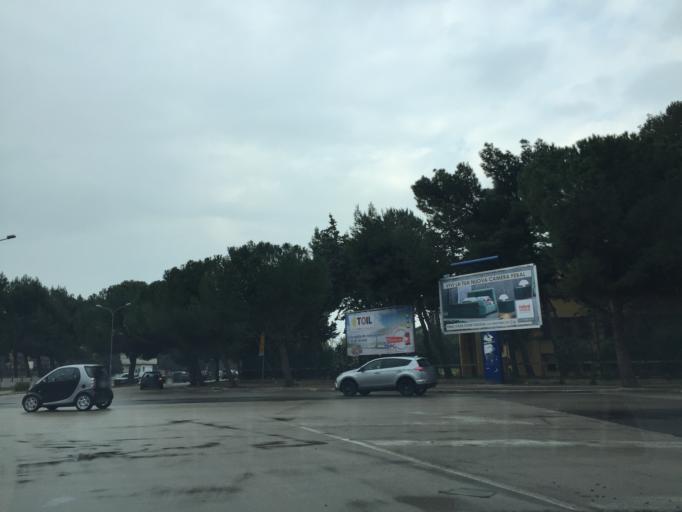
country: IT
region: Apulia
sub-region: Provincia di Foggia
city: Foggia
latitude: 41.4565
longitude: 15.5285
